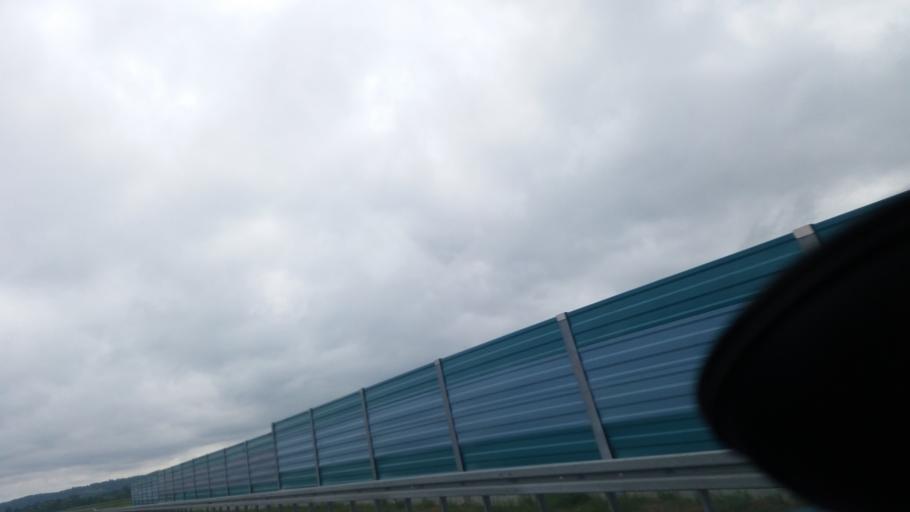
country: RS
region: Central Serbia
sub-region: Kolubarski Okrug
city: Ljig
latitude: 44.2971
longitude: 20.2345
